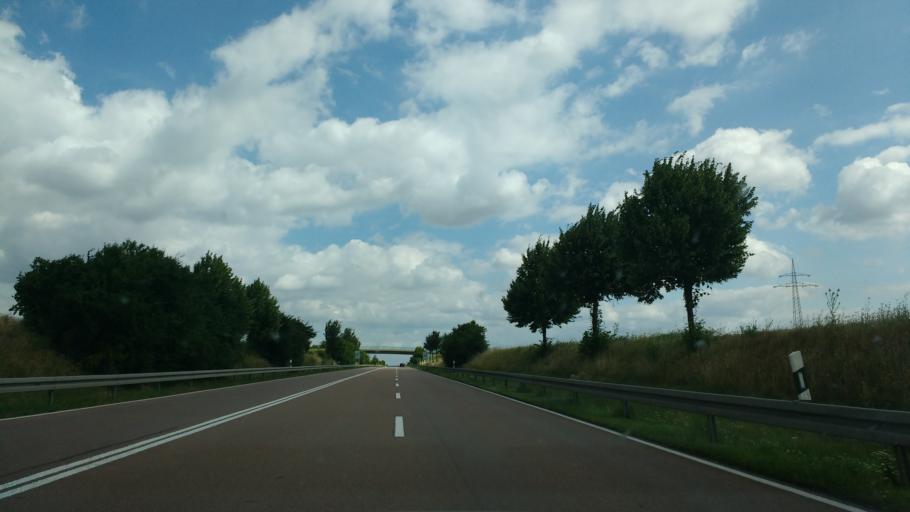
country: DE
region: Saxony-Anhalt
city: Theissen
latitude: 51.0672
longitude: 12.1067
